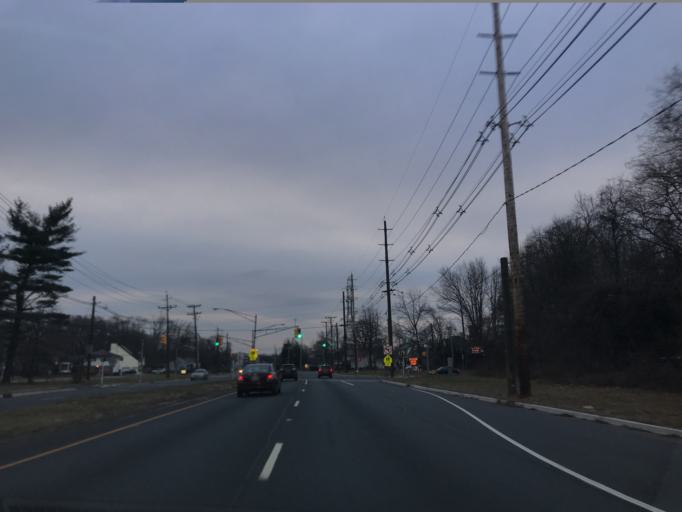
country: US
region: New Jersey
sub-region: Middlesex County
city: Milltown
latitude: 40.4499
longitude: -74.4622
